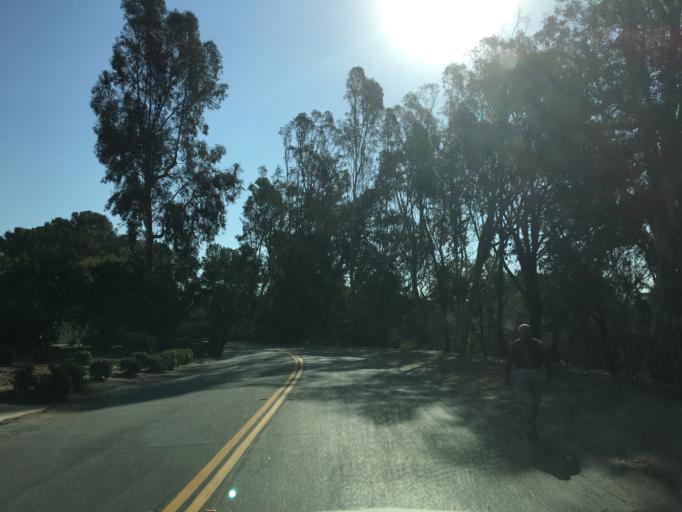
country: US
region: California
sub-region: Los Angeles County
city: Charter Oak
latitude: 34.0837
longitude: -117.8473
